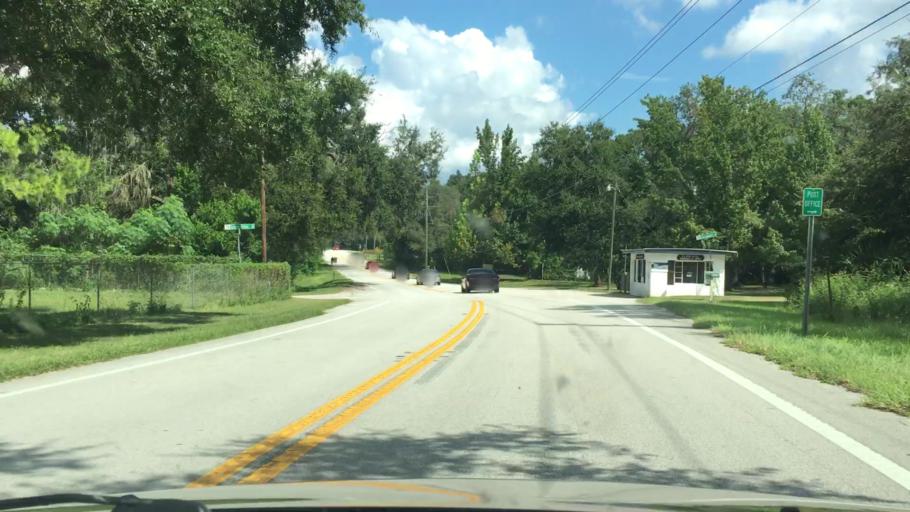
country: US
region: Florida
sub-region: Lake County
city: Montverde
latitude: 28.6189
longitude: -81.7031
